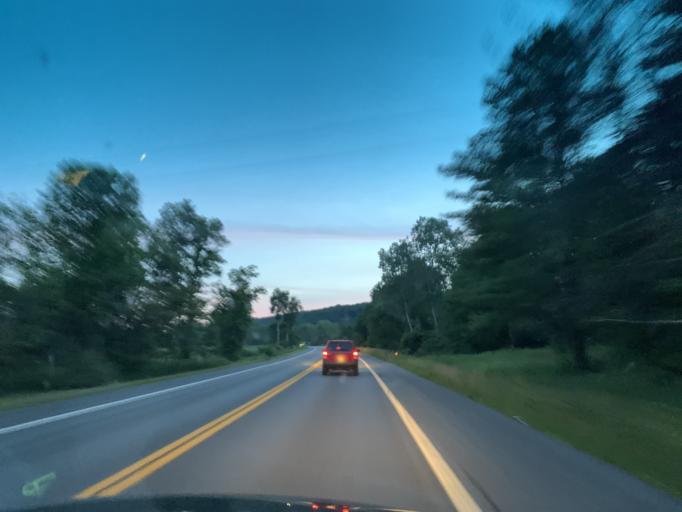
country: US
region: New York
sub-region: Chenango County
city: New Berlin
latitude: 42.5639
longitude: -75.3543
